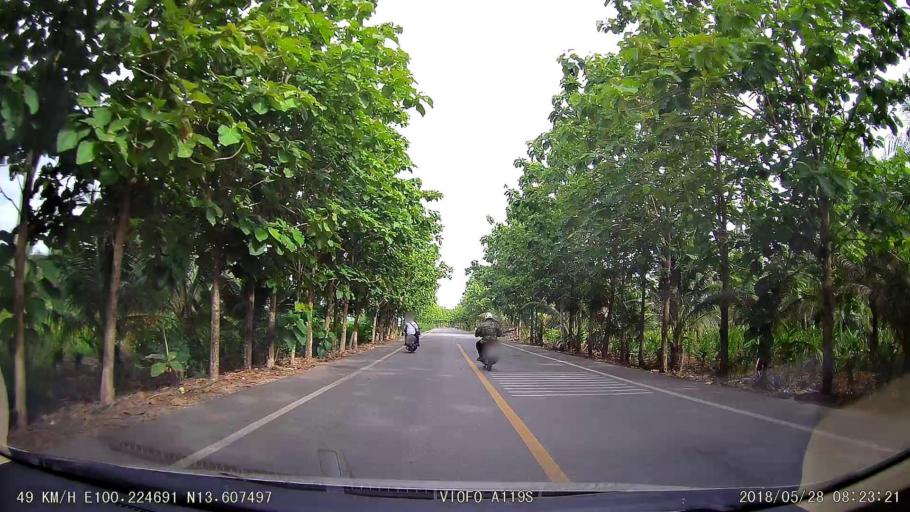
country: TH
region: Samut Sakhon
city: Krathum Baen
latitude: 13.6076
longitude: 100.2245
